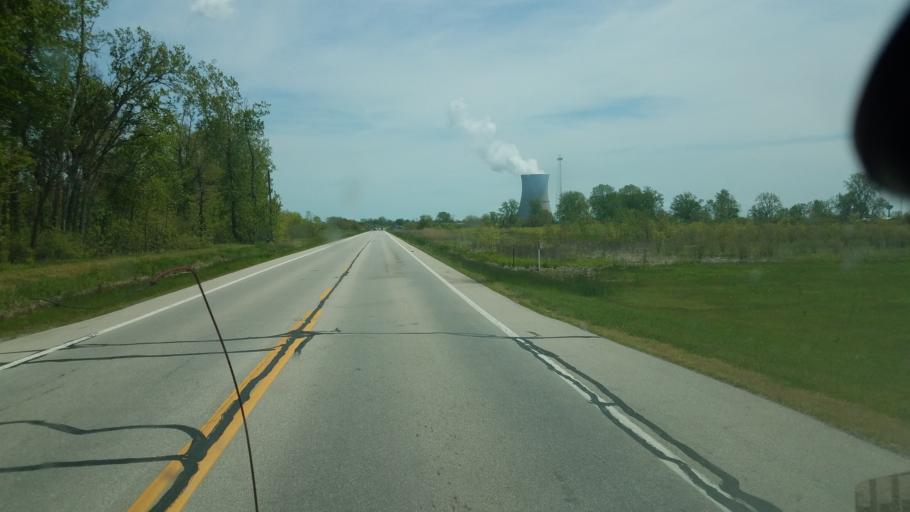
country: US
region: Ohio
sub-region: Ottawa County
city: Oak Harbor
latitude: 41.6038
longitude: -83.1159
